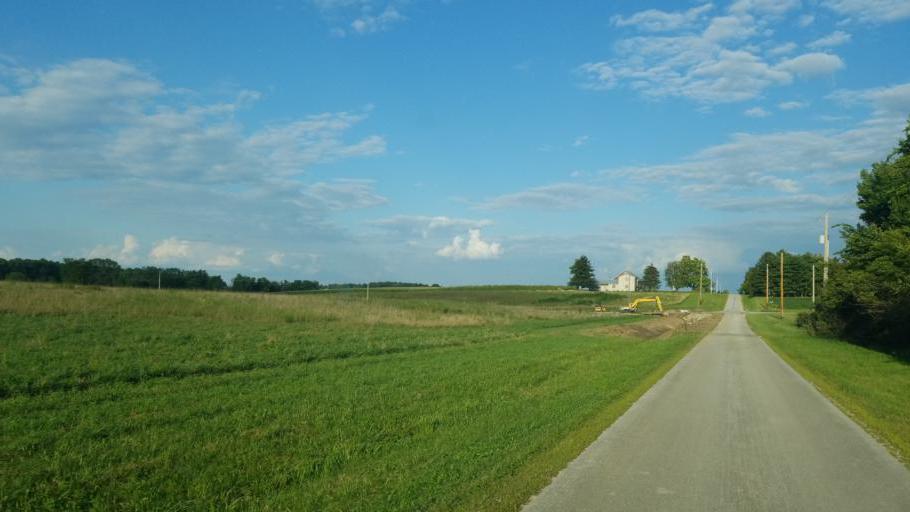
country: US
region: Ohio
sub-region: Sandusky County
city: Green Springs
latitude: 41.1103
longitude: -82.9788
